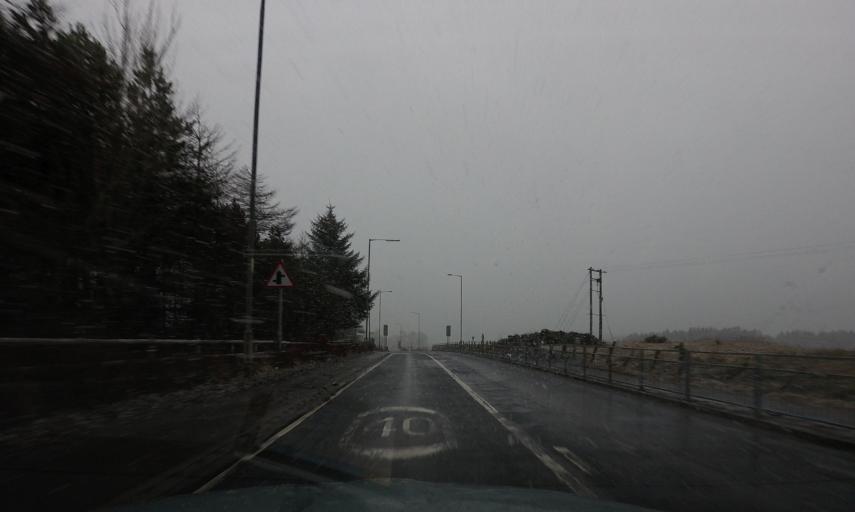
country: GB
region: Scotland
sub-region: North Lanarkshire
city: Caldercruix
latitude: 55.8461
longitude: -3.8588
